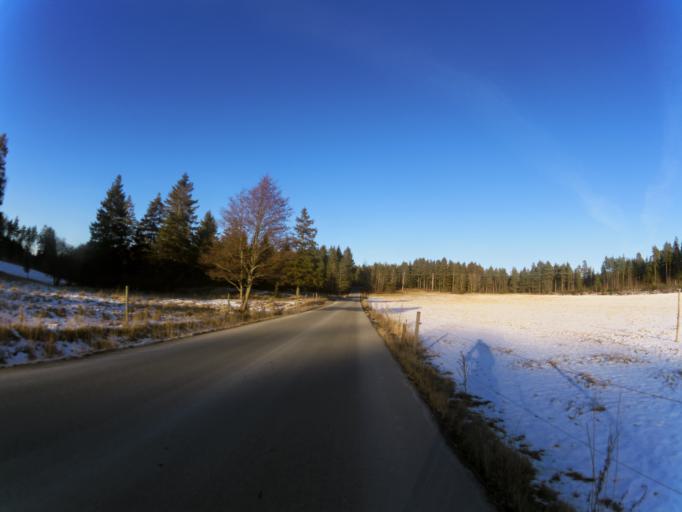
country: NO
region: Ostfold
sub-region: Fredrikstad
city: Lervik
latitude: 59.2579
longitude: 10.8046
